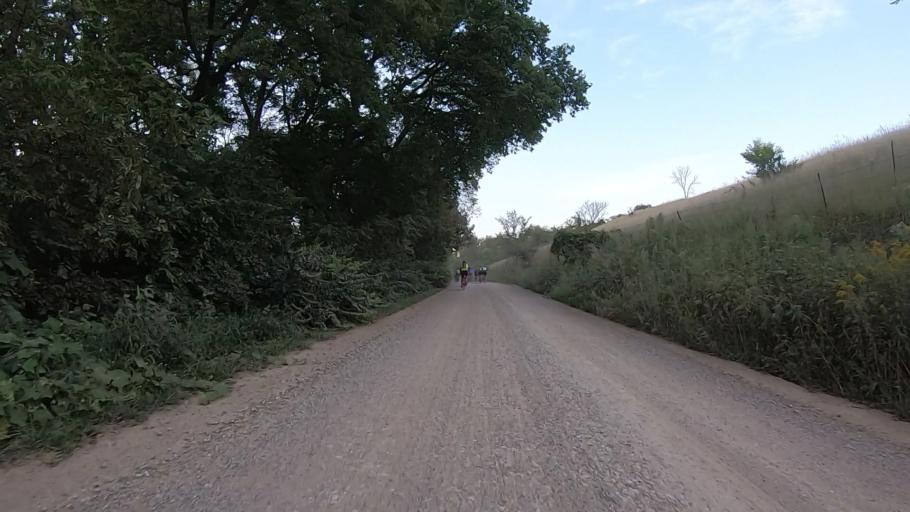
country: US
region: Kansas
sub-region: Marshall County
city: Marysville
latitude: 39.8361
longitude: -96.6655
